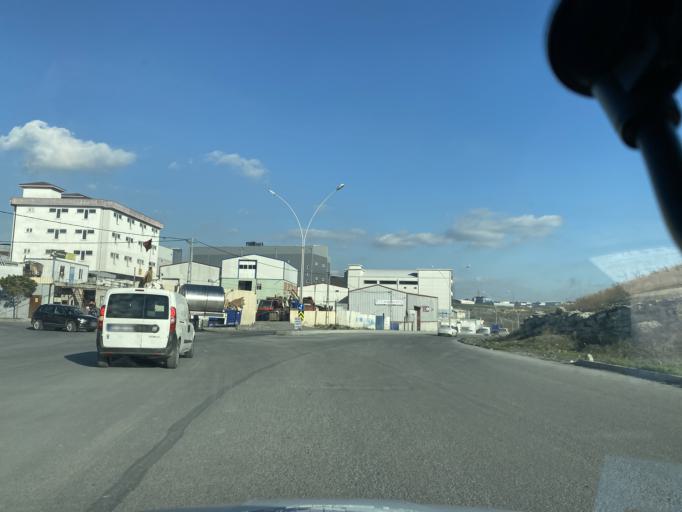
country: TR
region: Istanbul
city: Esenyurt
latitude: 41.0518
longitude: 28.6477
